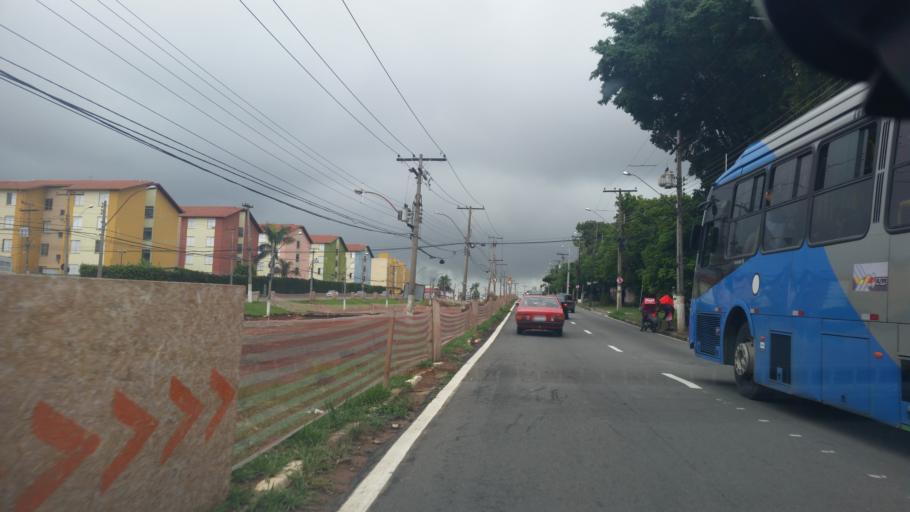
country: BR
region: Sao Paulo
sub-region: Campinas
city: Campinas
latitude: -22.9163
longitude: -47.1043
